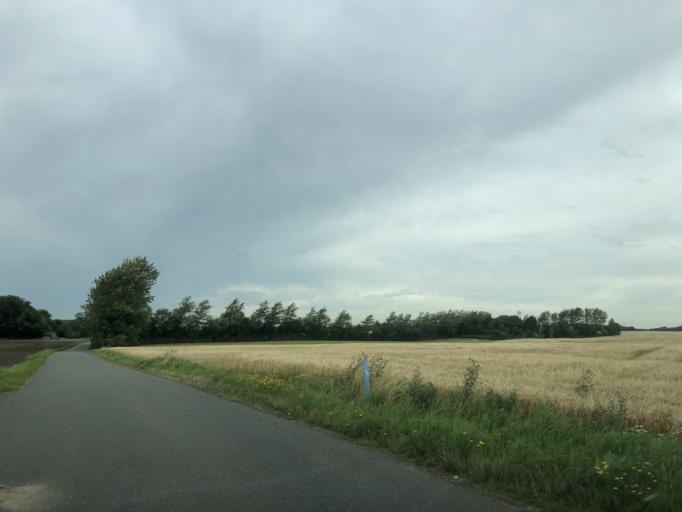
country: DK
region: Central Jutland
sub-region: Holstebro Kommune
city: Holstebro
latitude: 56.3945
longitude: 8.5977
